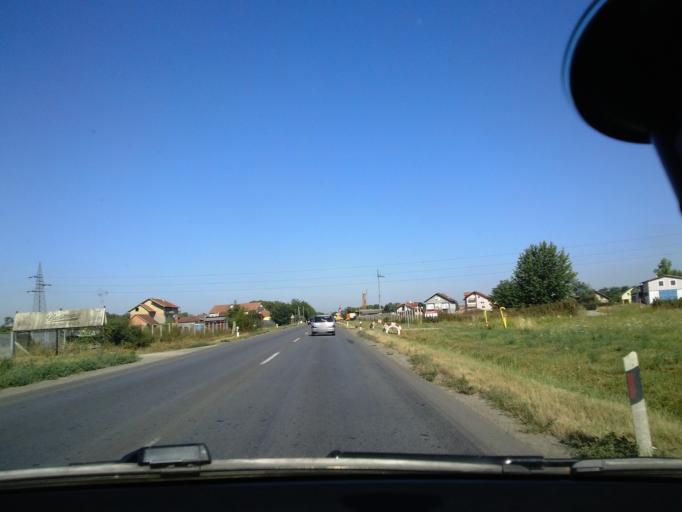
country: RS
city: Rumenka
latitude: 45.2880
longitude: 19.7554
